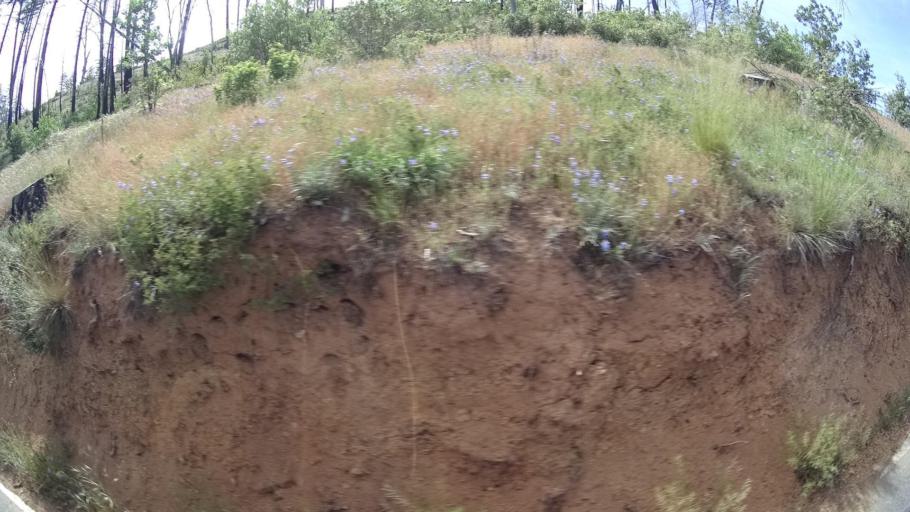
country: US
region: California
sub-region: Lake County
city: Cobb
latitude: 38.8483
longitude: -122.7226
